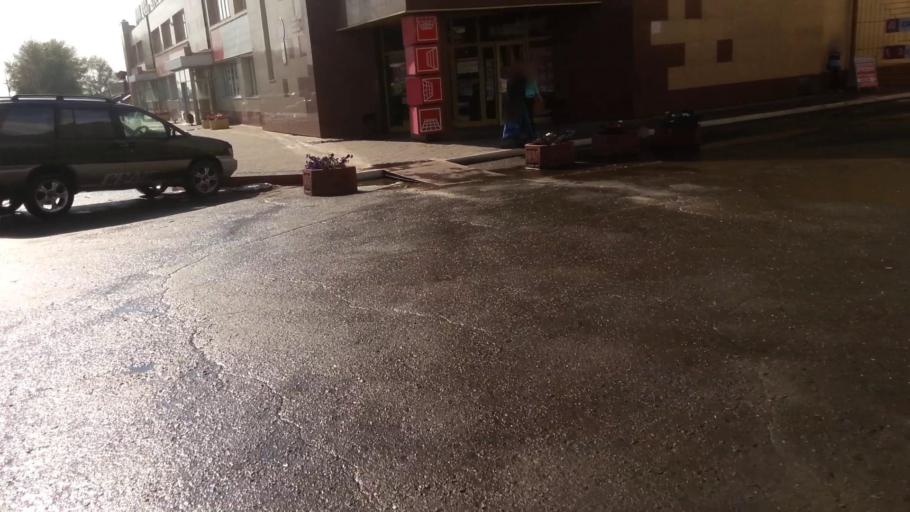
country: RU
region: Altai Krai
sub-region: Gorod Barnaulskiy
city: Barnaul
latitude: 53.3412
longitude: 83.7460
